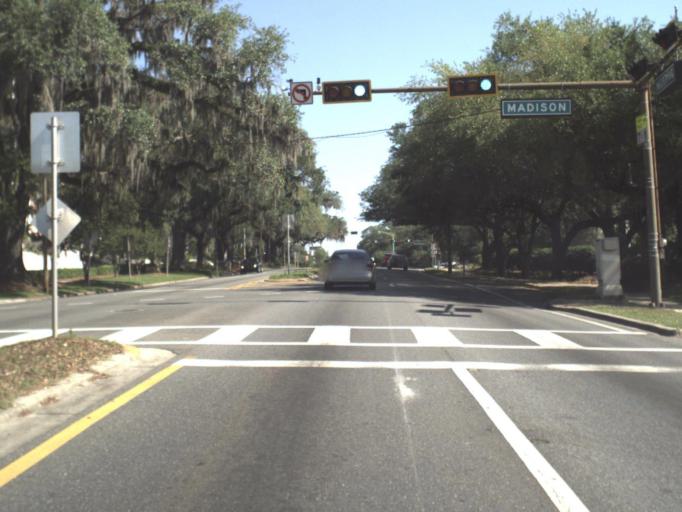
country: US
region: Florida
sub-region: Leon County
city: Tallahassee
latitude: 30.4364
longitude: -84.2806
